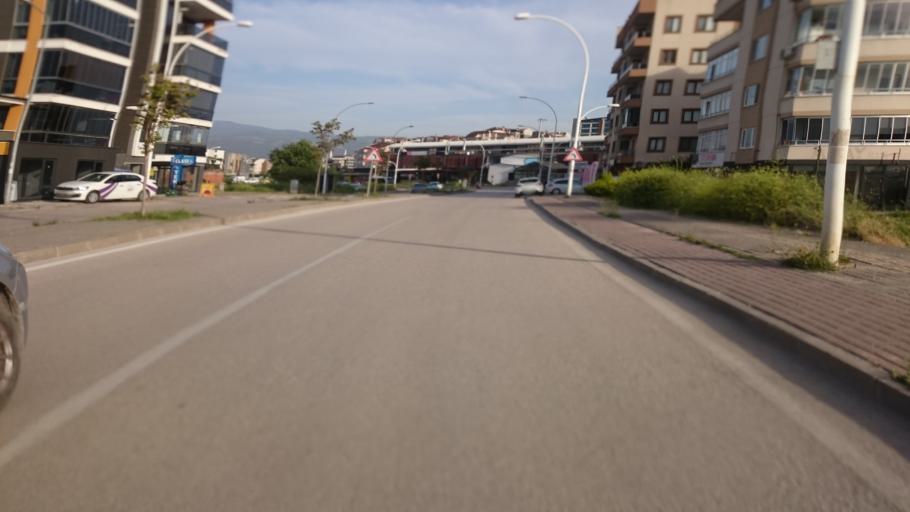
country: TR
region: Bursa
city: Cali
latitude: 40.2300
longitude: 28.9140
